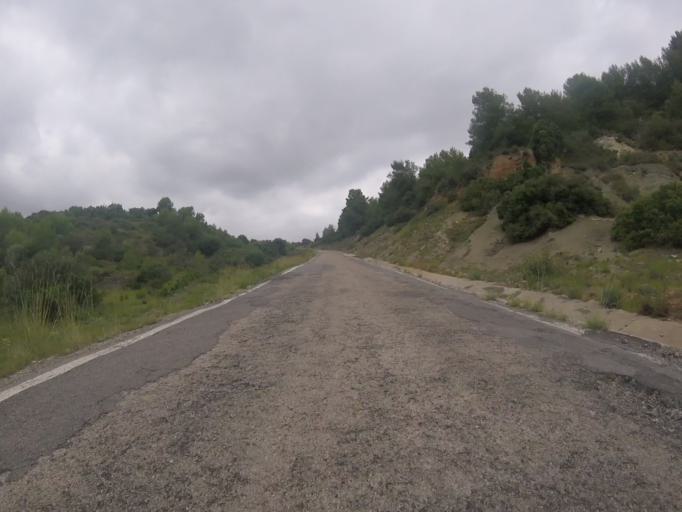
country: ES
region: Valencia
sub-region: Provincia de Castello
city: Cabanes
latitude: 40.1202
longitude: 0.0466
